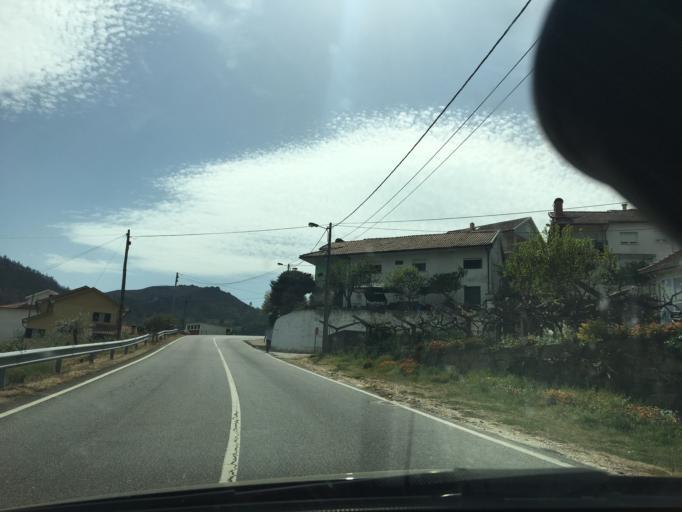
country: PT
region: Vila Real
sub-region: Boticas
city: Boticas
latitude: 41.6891
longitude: -7.6774
